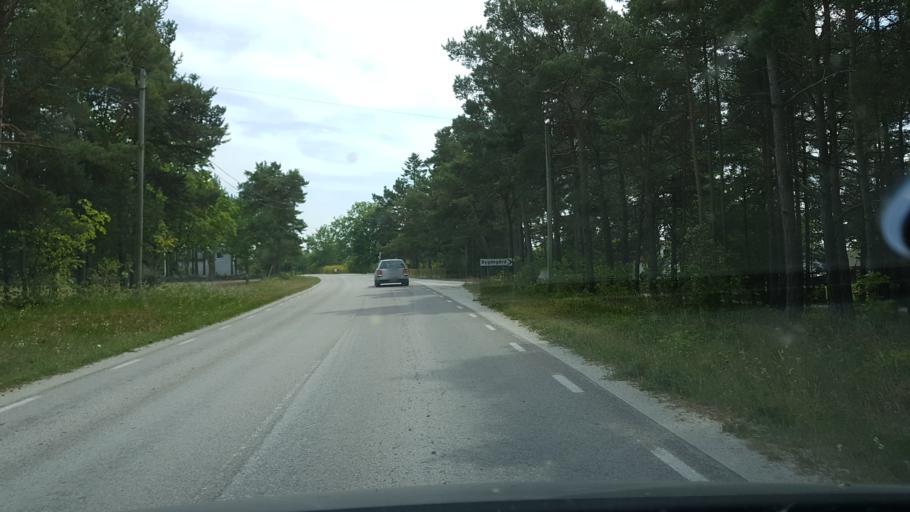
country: SE
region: Gotland
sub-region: Gotland
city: Slite
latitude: 57.7367
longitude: 18.7375
